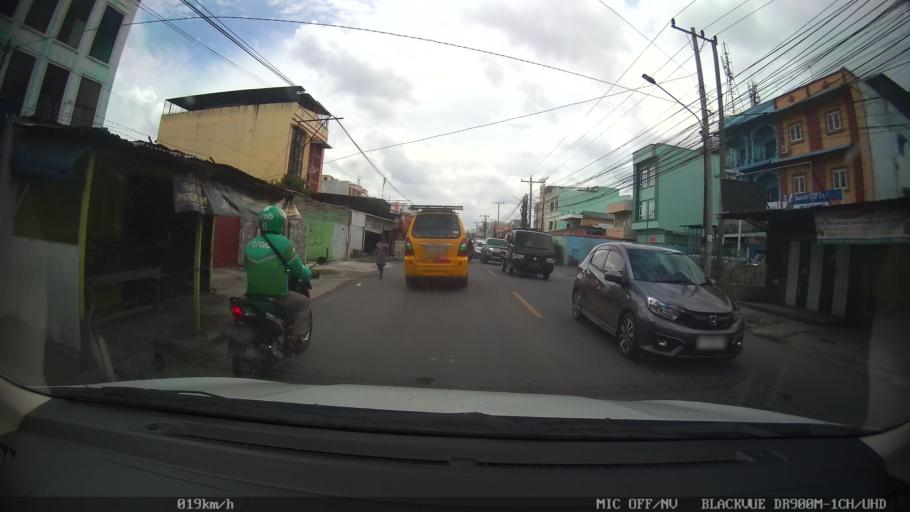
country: ID
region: North Sumatra
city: Medan
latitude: 3.6214
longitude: 98.7076
